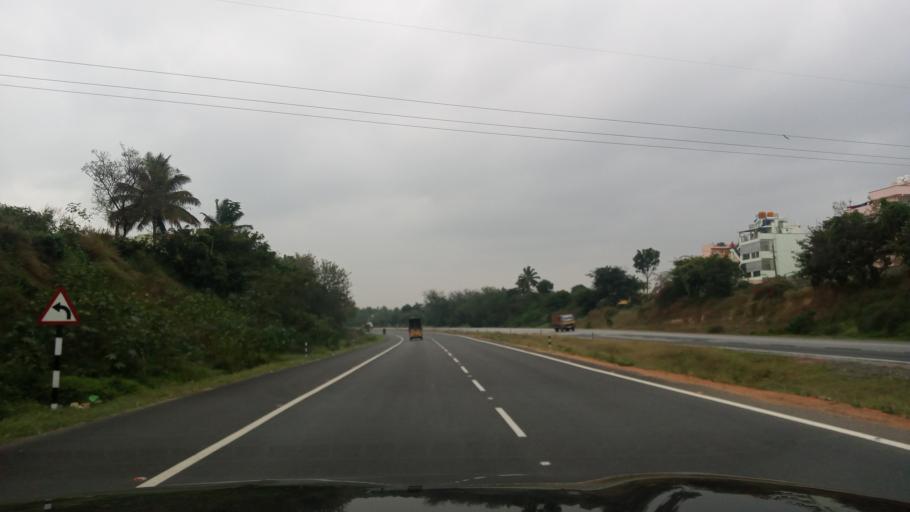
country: IN
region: Karnataka
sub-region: Bangalore Urban
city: Bangalore
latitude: 12.9859
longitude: 77.4714
